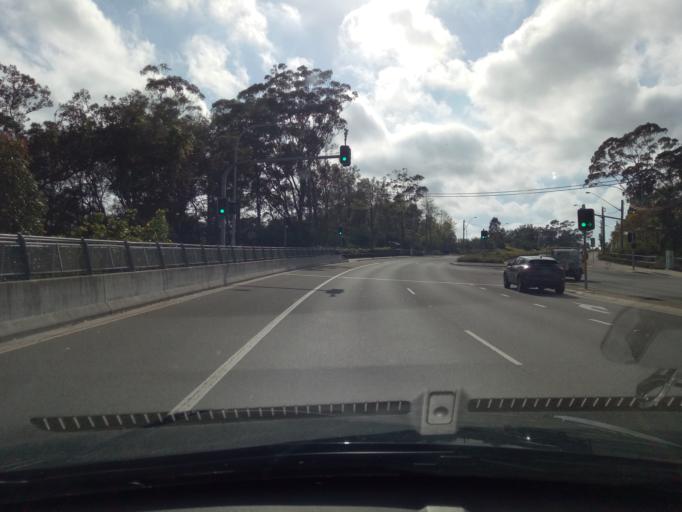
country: AU
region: New South Wales
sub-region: Gosford Shire
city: Holgate
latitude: -33.4243
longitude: 151.4269
